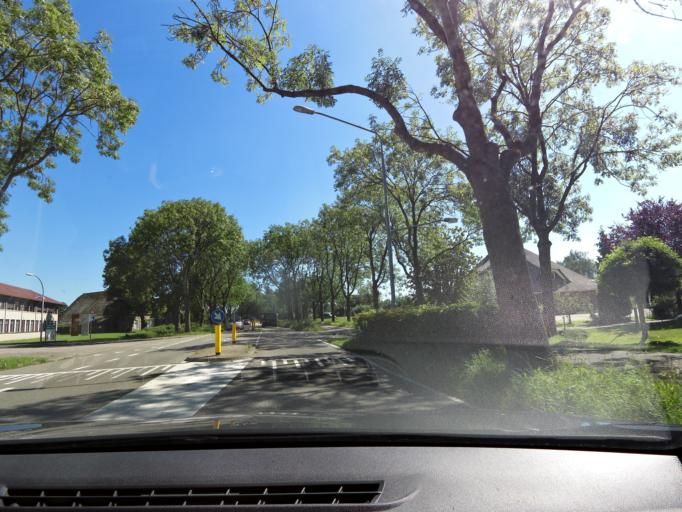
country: NL
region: South Holland
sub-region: Gemeente Dordrecht
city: Dordrecht
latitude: 51.7938
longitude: 4.7189
